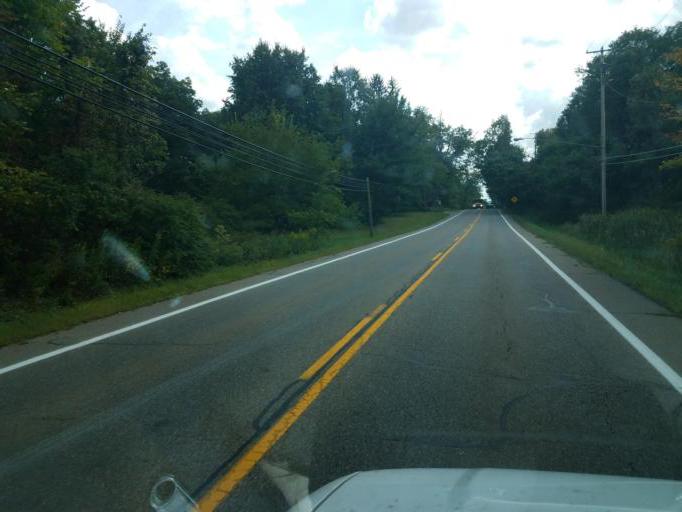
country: US
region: Ohio
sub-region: Portage County
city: Ravenna
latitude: 41.0947
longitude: -81.2427
